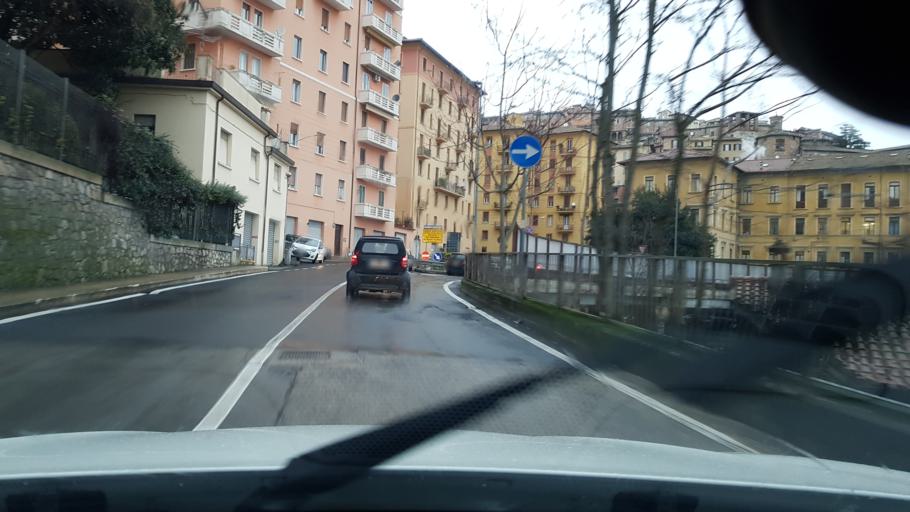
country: IT
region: Umbria
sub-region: Provincia di Perugia
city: Perugia
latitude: 43.1094
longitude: 12.3915
